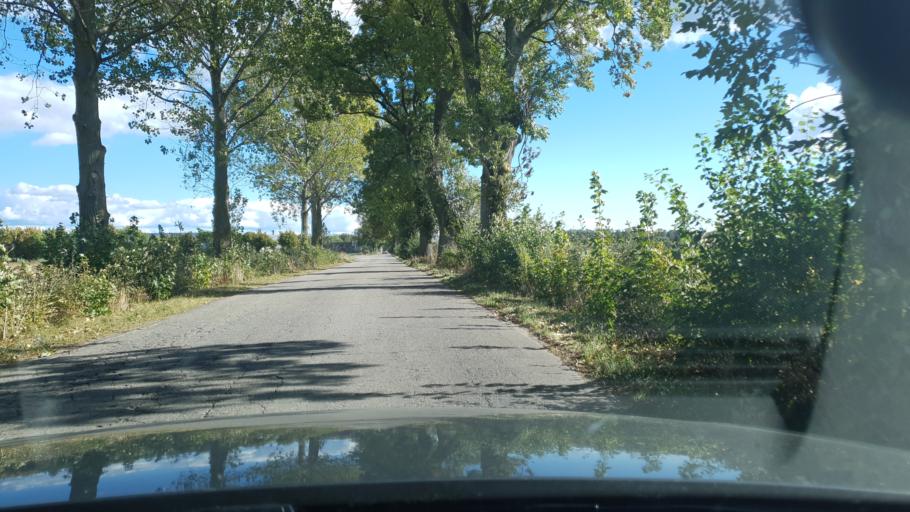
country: PL
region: Pomeranian Voivodeship
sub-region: Powiat pucki
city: Zelistrzewo
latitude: 54.6871
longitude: 18.4462
